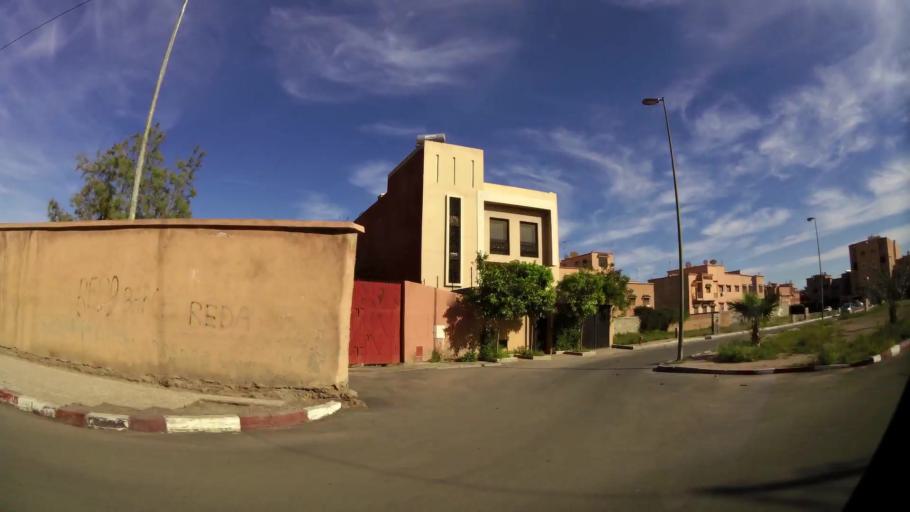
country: MA
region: Marrakech-Tensift-Al Haouz
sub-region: Marrakech
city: Marrakesh
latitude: 31.6567
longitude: -8.0118
